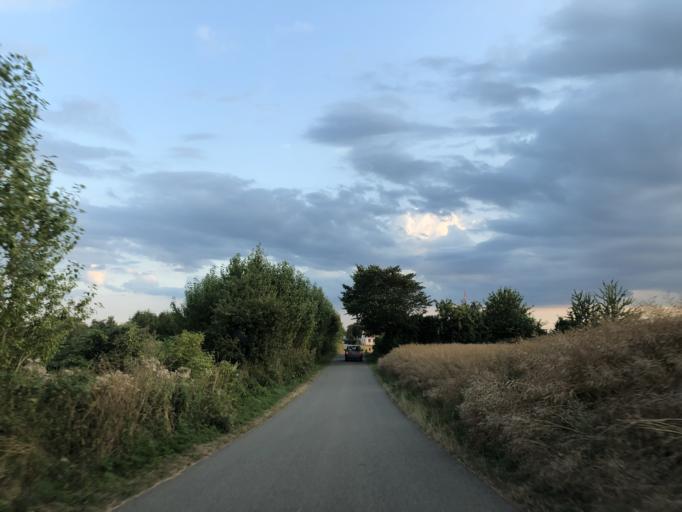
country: DK
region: South Denmark
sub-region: Kerteminde Kommune
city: Munkebo
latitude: 55.5159
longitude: 10.5963
